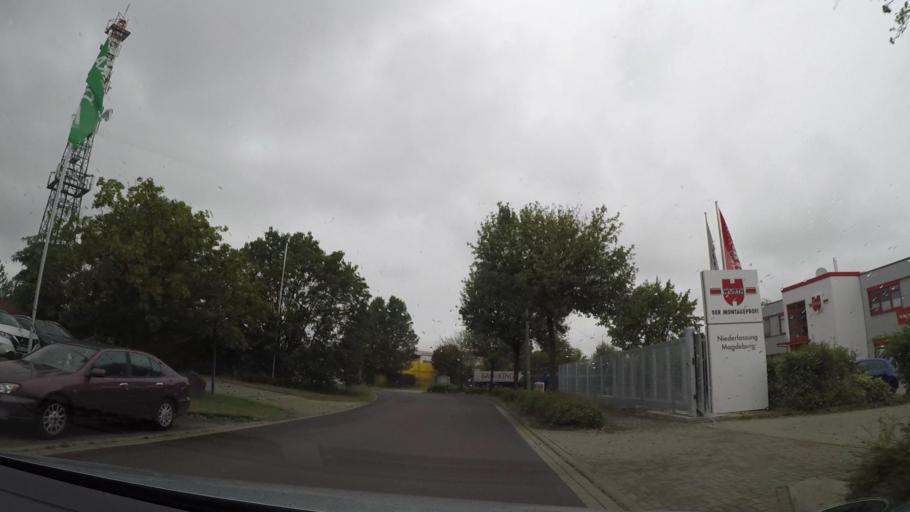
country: DE
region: Saxony-Anhalt
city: Neue Neustadt
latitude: 52.1661
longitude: 11.6039
